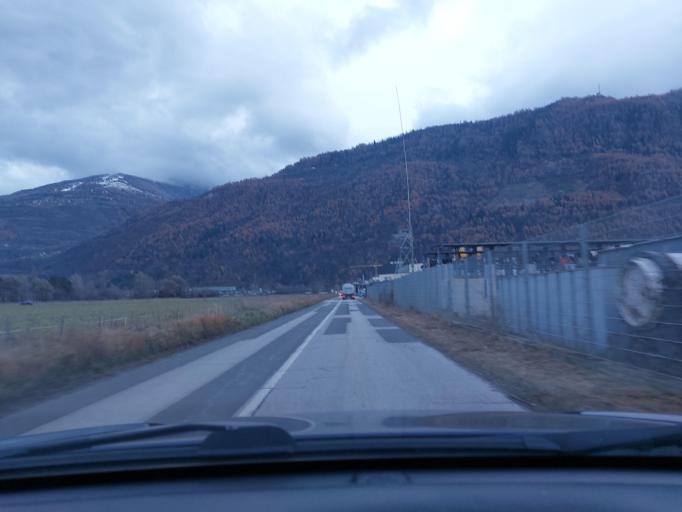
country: CH
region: Valais
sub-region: Conthey District
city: Vetroz
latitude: 46.2074
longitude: 7.2812
